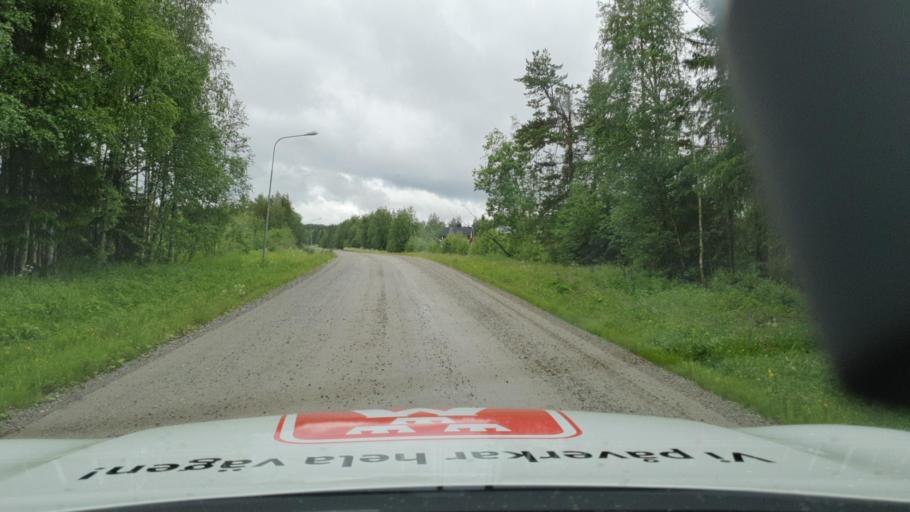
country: SE
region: Vaesterbotten
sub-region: Dorotea Kommun
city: Dorotea
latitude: 64.0914
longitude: 16.6665
